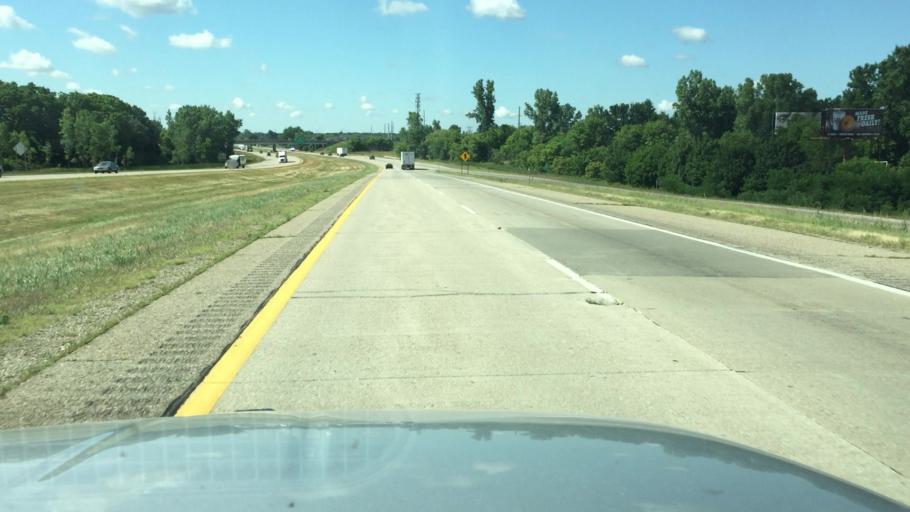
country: US
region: Michigan
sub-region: Eaton County
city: Charlotte
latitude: 42.5740
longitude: -84.8202
